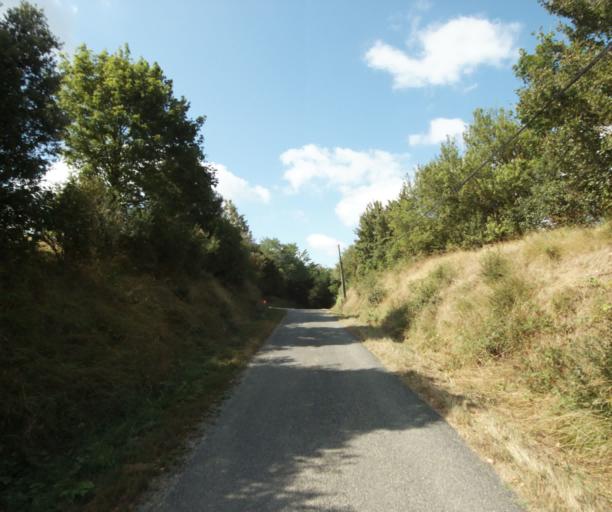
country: FR
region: Midi-Pyrenees
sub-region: Departement de la Haute-Garonne
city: Saint-Felix-Lauragais
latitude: 43.4467
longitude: 1.8266
